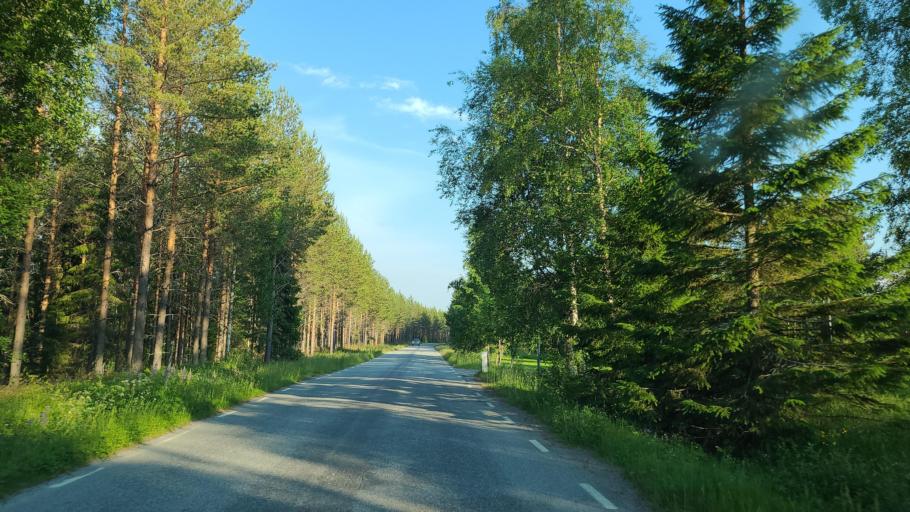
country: SE
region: Vaesterbotten
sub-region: Skelleftea Kommun
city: Burea
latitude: 64.3628
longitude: 21.3316
